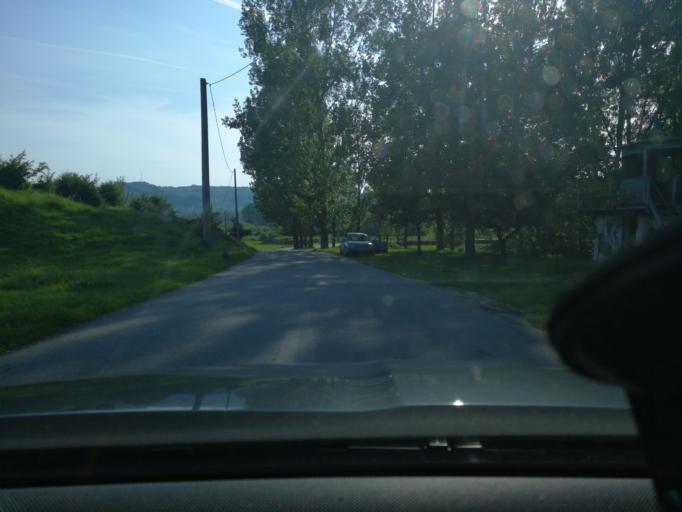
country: RO
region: Prahova
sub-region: Municipiul Campina
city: Campina
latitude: 45.1473
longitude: 25.7280
